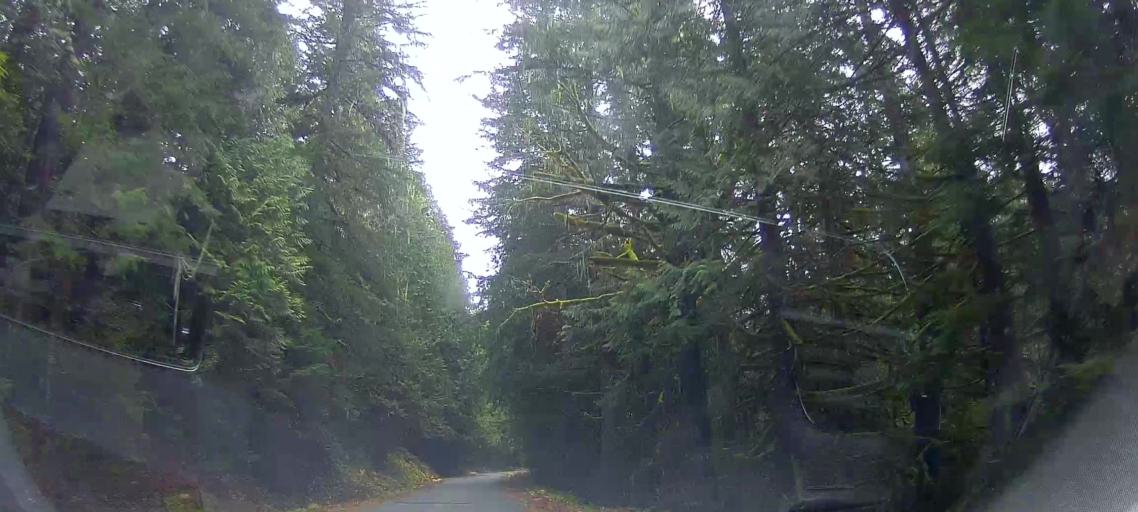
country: US
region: Washington
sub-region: Snohomish County
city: Darrington
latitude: 48.5251
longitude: -121.3863
